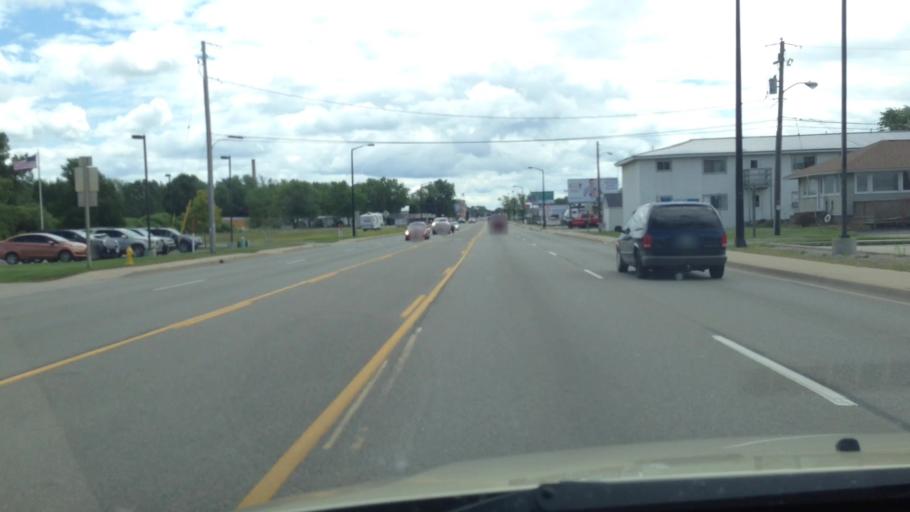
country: US
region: Michigan
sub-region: Menominee County
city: Menominee
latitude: 45.1327
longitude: -87.6127
